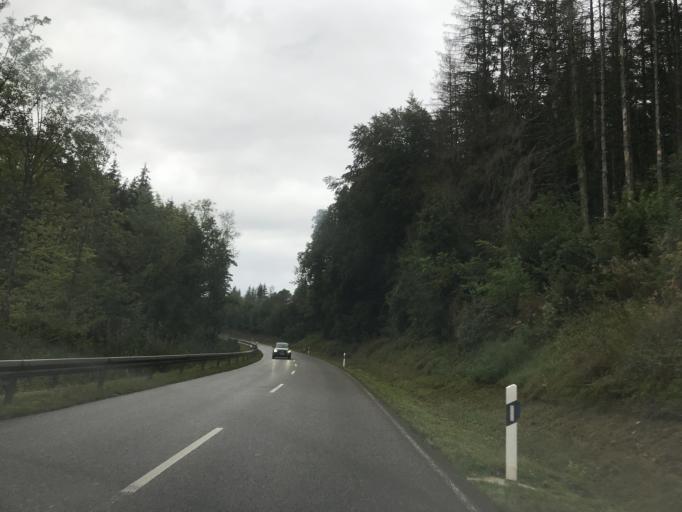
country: DE
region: Baden-Wuerttemberg
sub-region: Freiburg Region
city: Schworstadt
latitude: 47.6110
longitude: 7.8654
